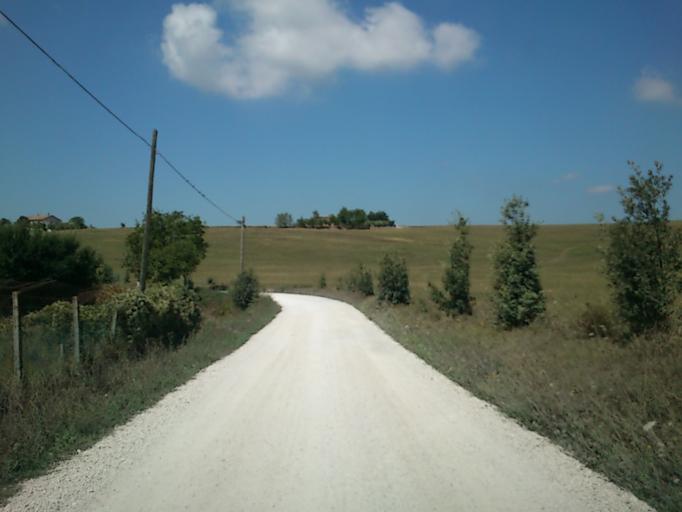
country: IT
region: The Marches
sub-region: Provincia di Pesaro e Urbino
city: Lucrezia
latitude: 43.7791
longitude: 12.9265
